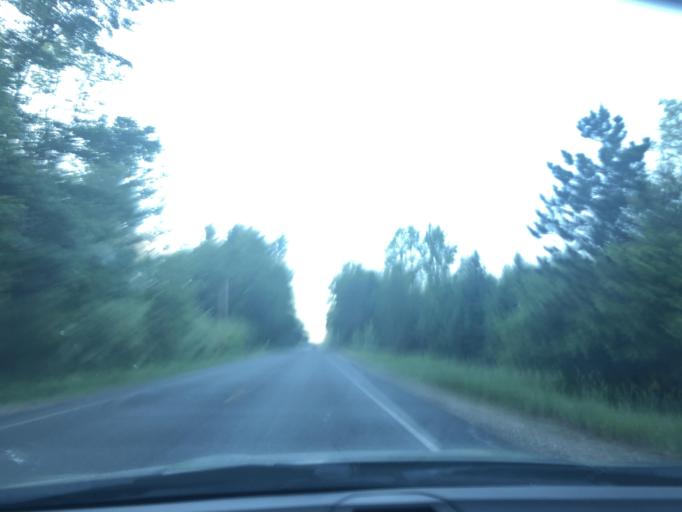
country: US
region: Michigan
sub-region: Missaukee County
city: Lake City
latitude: 44.3527
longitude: -85.0758
